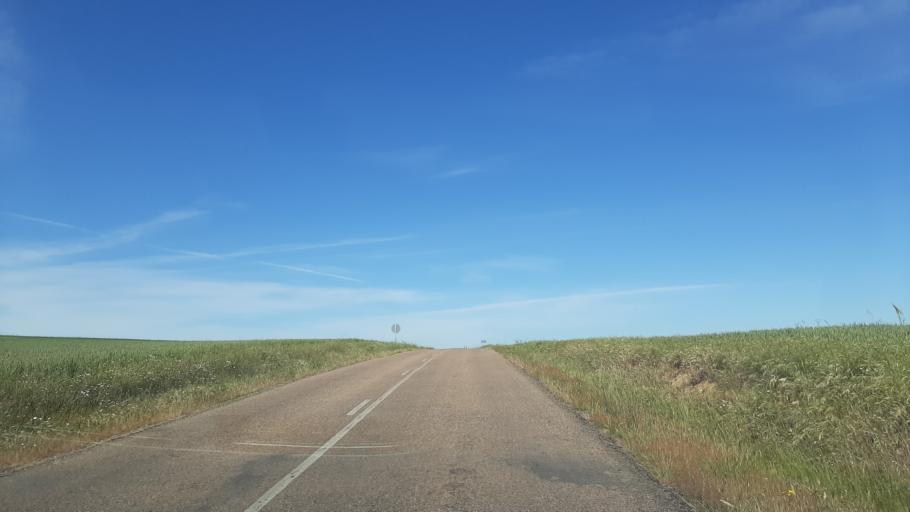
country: ES
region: Castille and Leon
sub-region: Provincia de Salamanca
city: Aldeaseca de Alba
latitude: 40.8181
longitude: -5.4576
